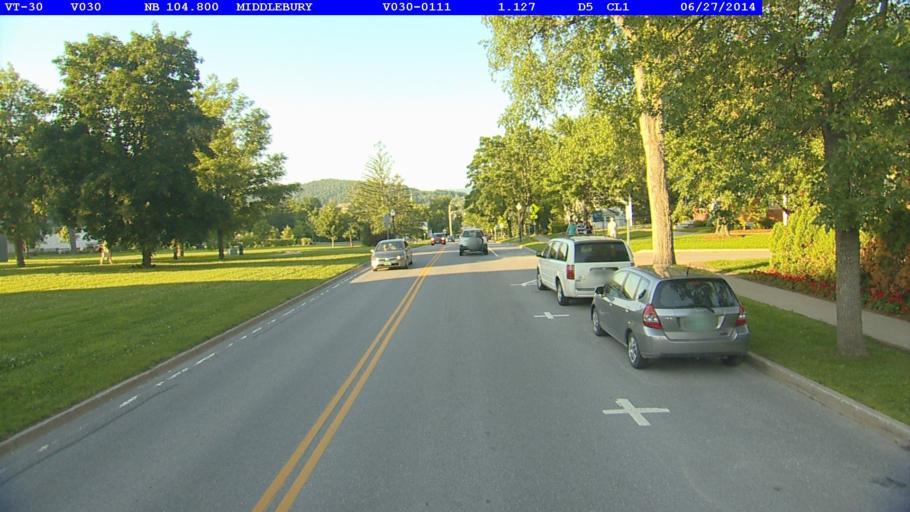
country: US
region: Vermont
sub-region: Addison County
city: Middlebury (village)
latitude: 44.0076
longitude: -73.1747
